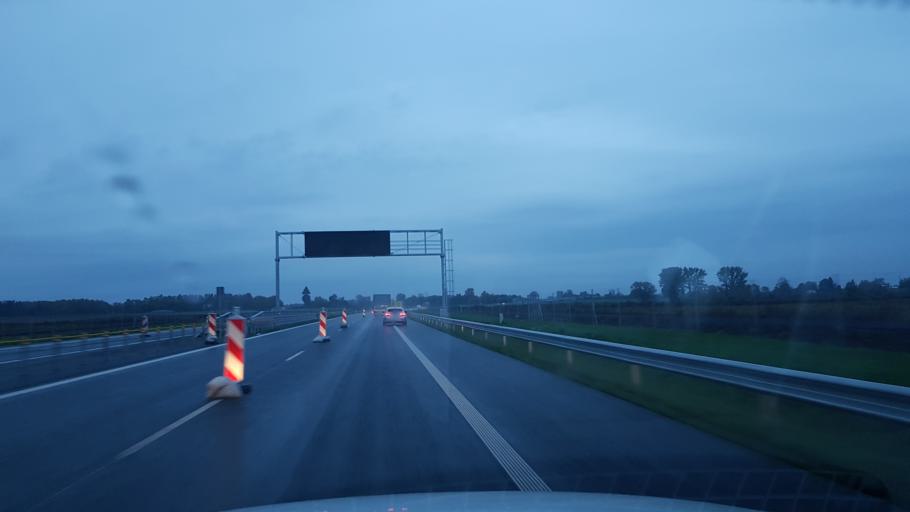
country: PL
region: West Pomeranian Voivodeship
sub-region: Powiat gryficki
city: Ploty
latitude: 53.8035
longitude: 15.2505
